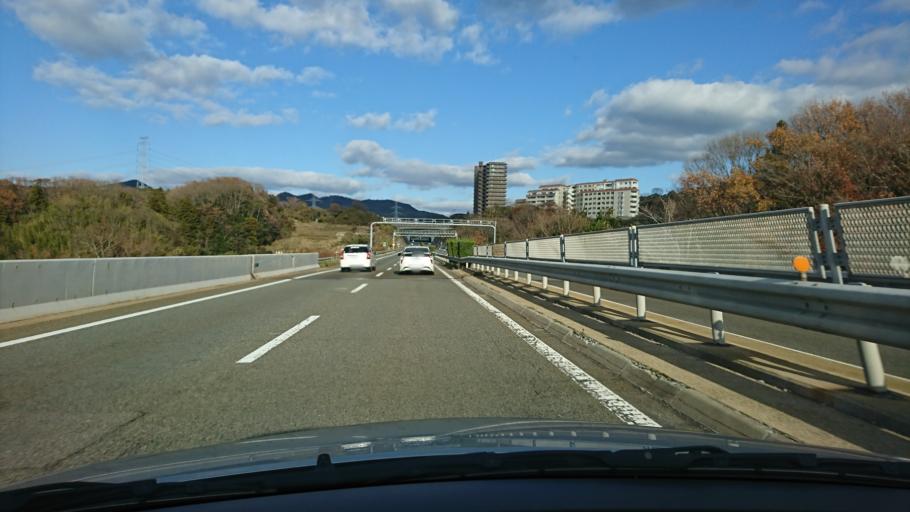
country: JP
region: Hyogo
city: Kobe
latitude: 34.7501
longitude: 135.1373
